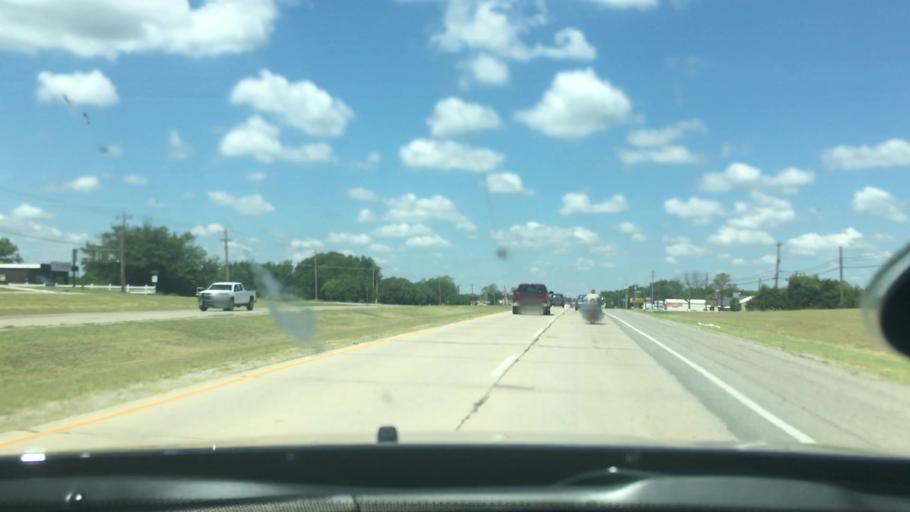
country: US
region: Oklahoma
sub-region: Carter County
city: Lone Grove
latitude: 34.1729
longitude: -97.2503
